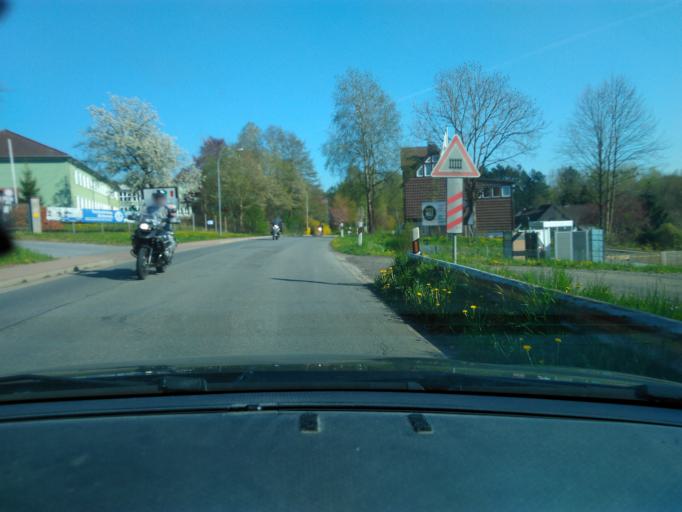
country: DE
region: Lower Saxony
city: Osterode am Harz
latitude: 51.7195
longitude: 10.2704
